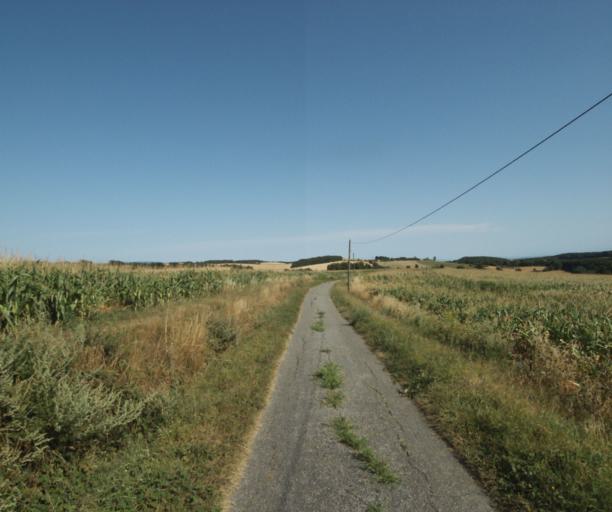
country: FR
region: Midi-Pyrenees
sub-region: Departement de la Haute-Garonne
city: Avignonet-Lauragais
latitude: 43.4273
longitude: 1.8230
